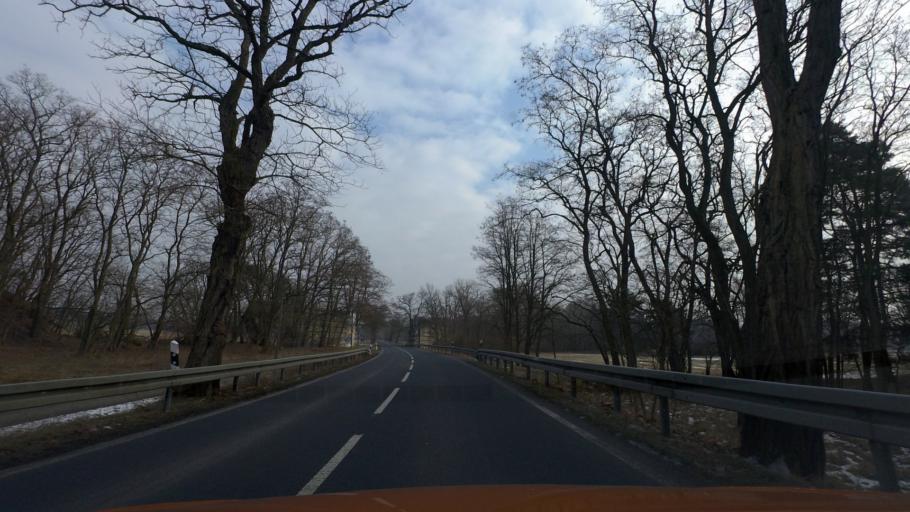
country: DE
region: Brandenburg
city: Rangsdorf
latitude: 52.2452
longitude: 13.4086
